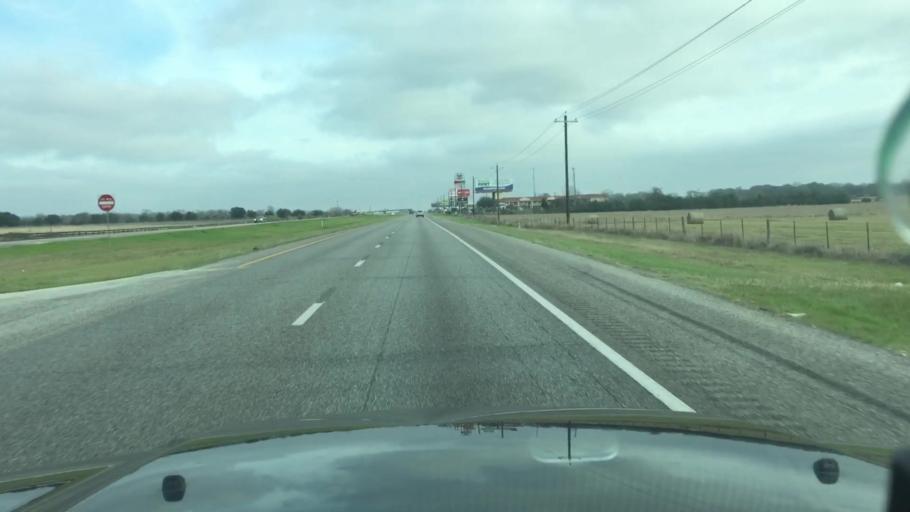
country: US
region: Texas
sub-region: Waller County
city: Hempstead
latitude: 30.1191
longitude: -96.0961
